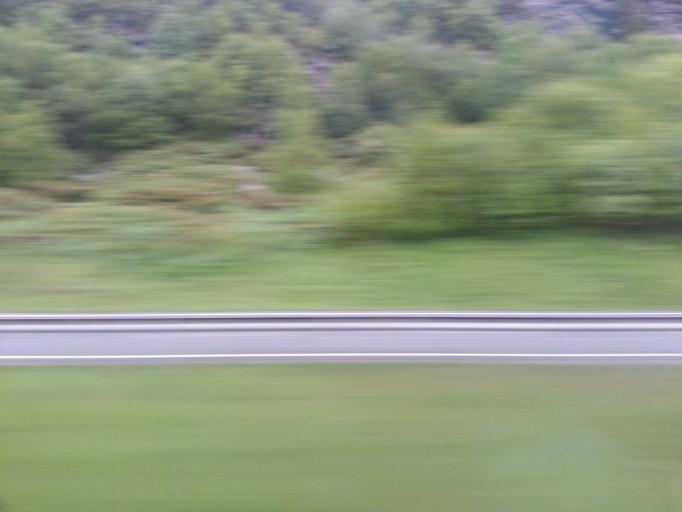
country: NO
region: Sor-Trondelag
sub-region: Oppdal
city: Oppdal
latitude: 62.4393
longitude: 9.6010
